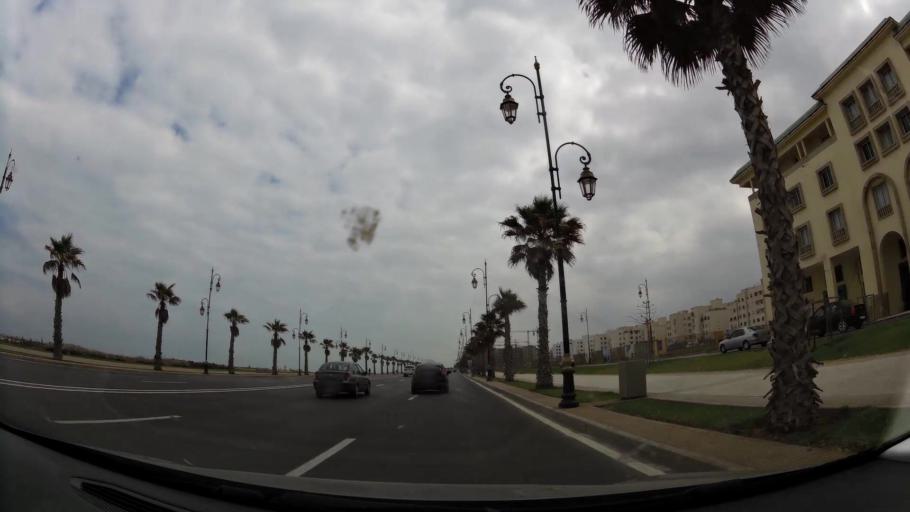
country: MA
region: Rabat-Sale-Zemmour-Zaer
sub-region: Rabat
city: Rabat
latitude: 33.9973
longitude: -6.8780
